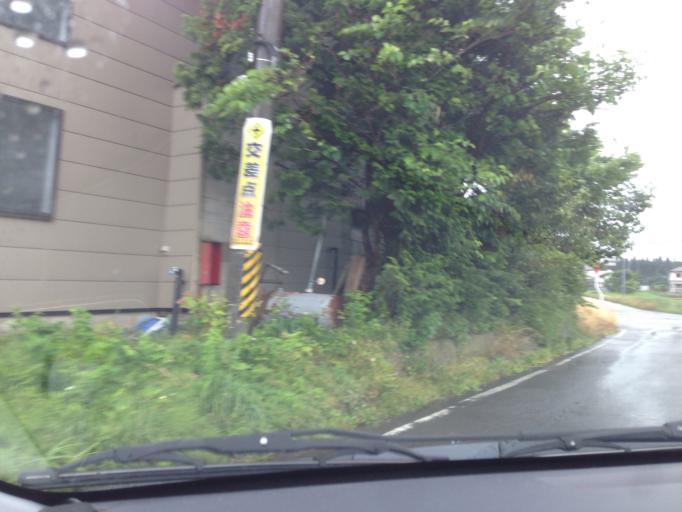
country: JP
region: Fukushima
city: Inawashiro
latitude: 37.5629
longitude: 140.0047
